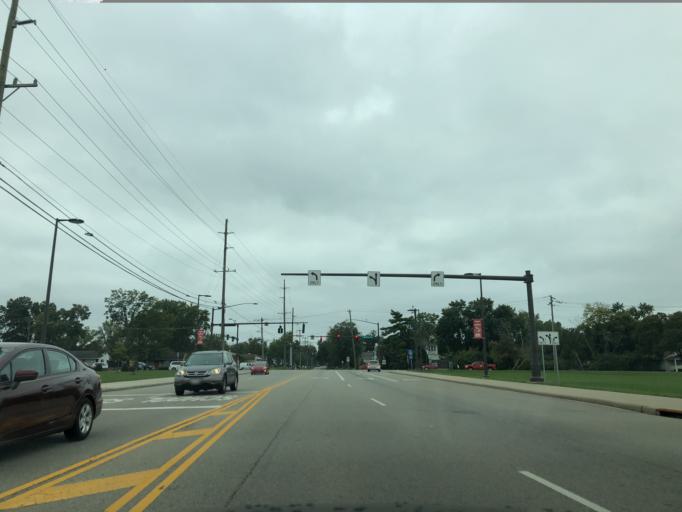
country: US
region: Ohio
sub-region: Hamilton County
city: Glendale
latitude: 39.2718
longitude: -84.4445
